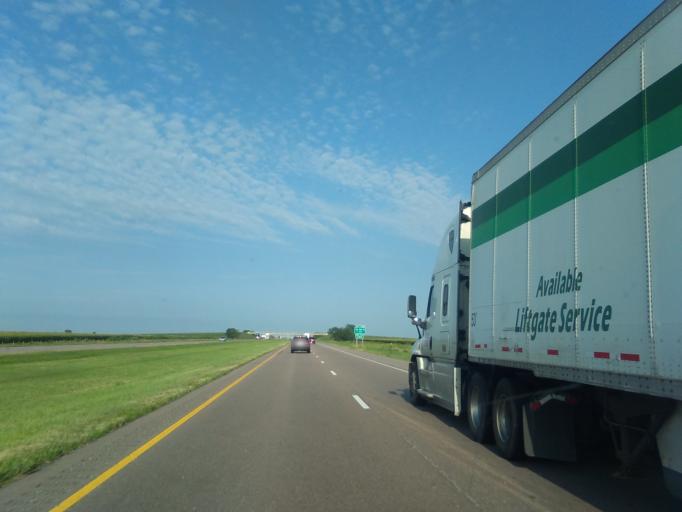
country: US
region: Nebraska
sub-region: York County
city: York
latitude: 40.8214
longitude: -97.7197
